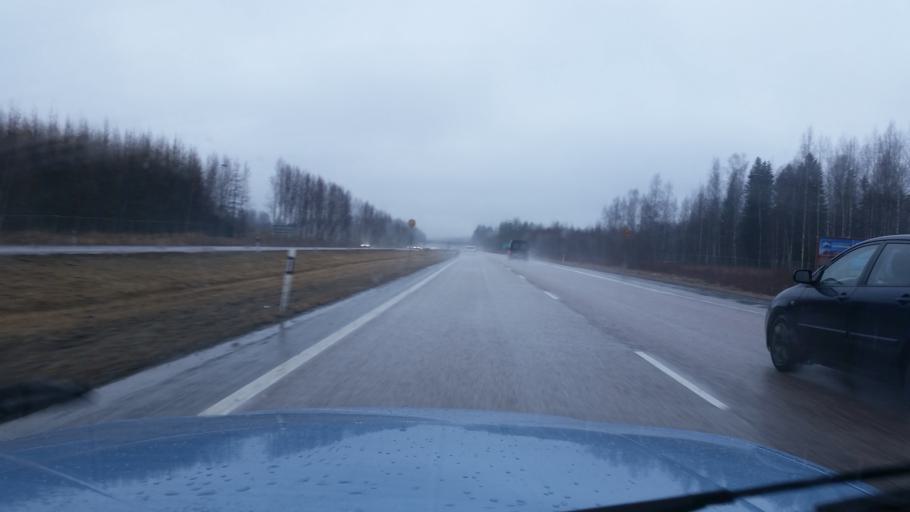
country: FI
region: Uusimaa
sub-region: Helsinki
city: Hyvinge
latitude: 60.6250
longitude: 24.8096
